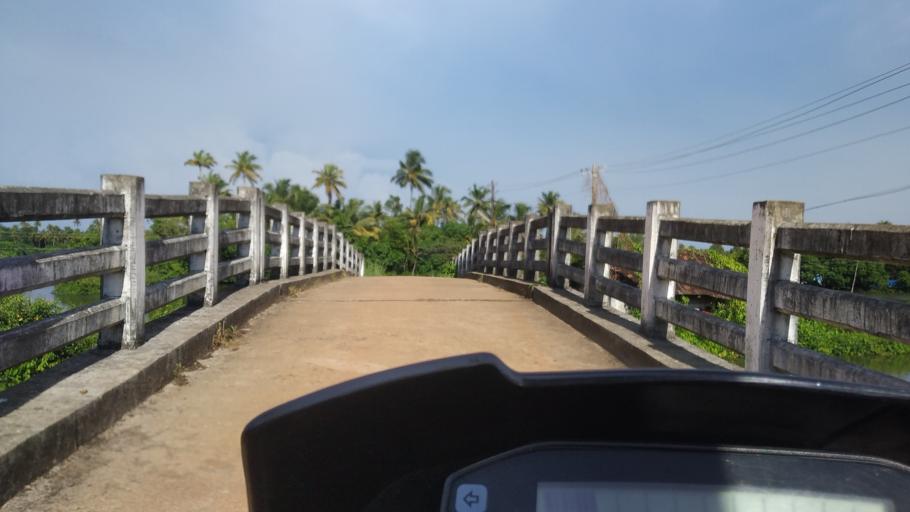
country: IN
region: Kerala
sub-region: Ernakulam
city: Elur
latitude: 10.0763
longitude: 76.2168
